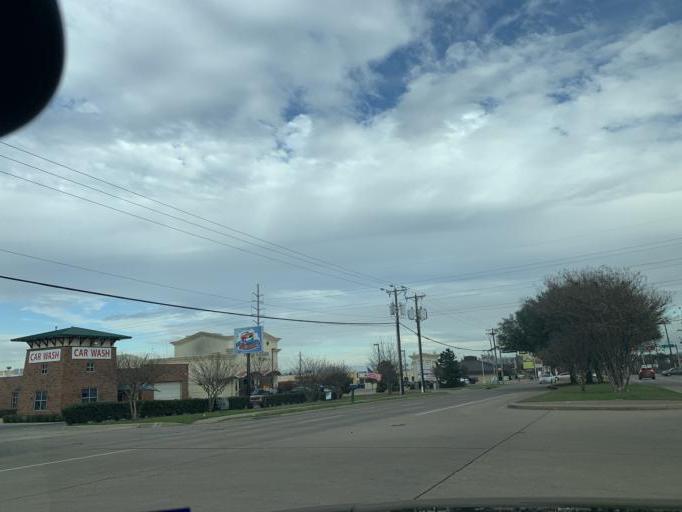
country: US
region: Texas
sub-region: Dallas County
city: Cedar Hill
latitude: 32.5899
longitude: -96.9437
